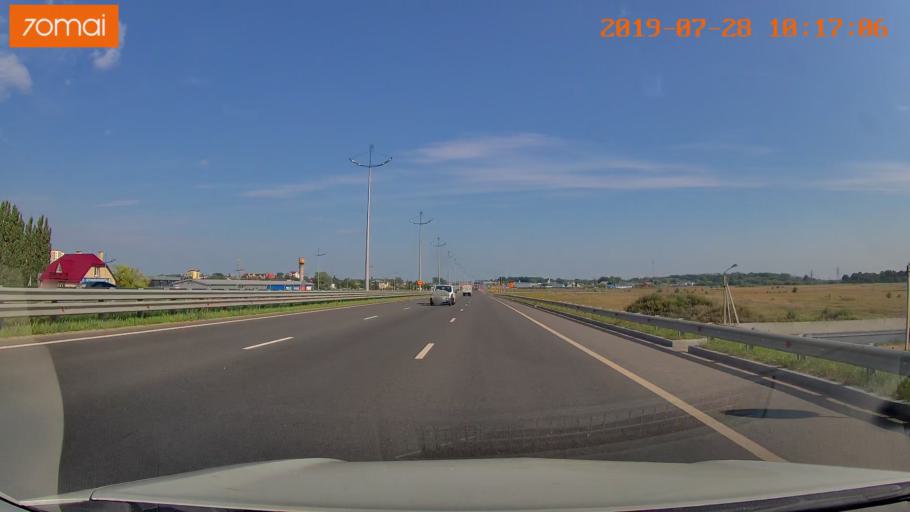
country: RU
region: Kaliningrad
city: Maloye Isakovo
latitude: 54.7354
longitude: 20.5964
